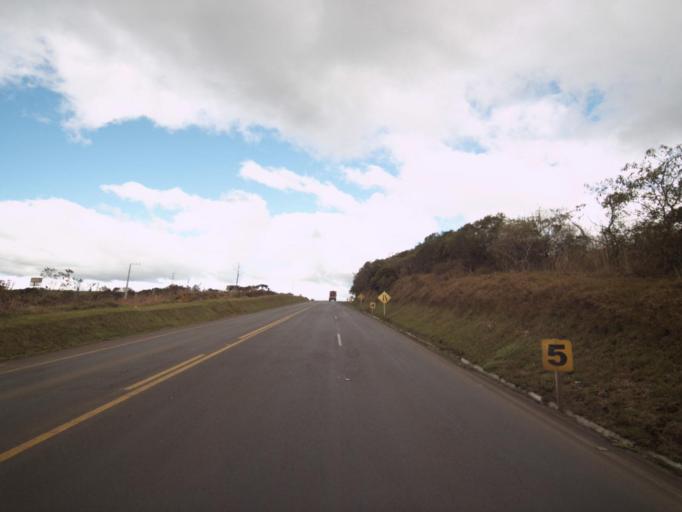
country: BR
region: Santa Catarina
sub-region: Joacaba
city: Joacaba
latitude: -27.0956
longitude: -51.6555
